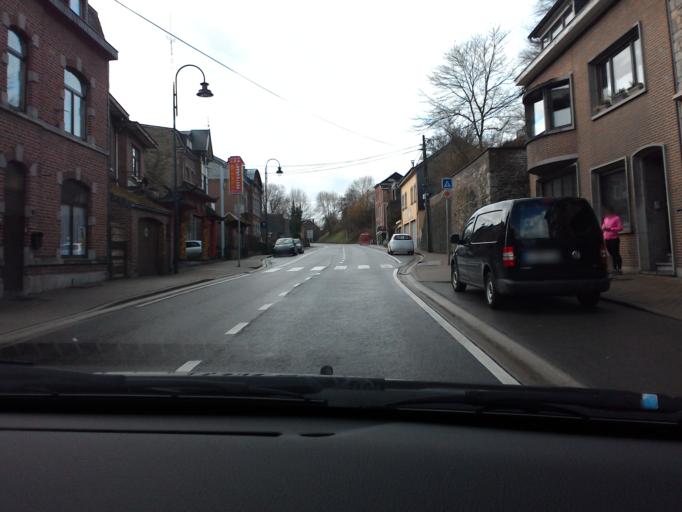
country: BE
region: Wallonia
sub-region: Province de Liege
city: Stavelot
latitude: 50.3913
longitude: 5.9247
